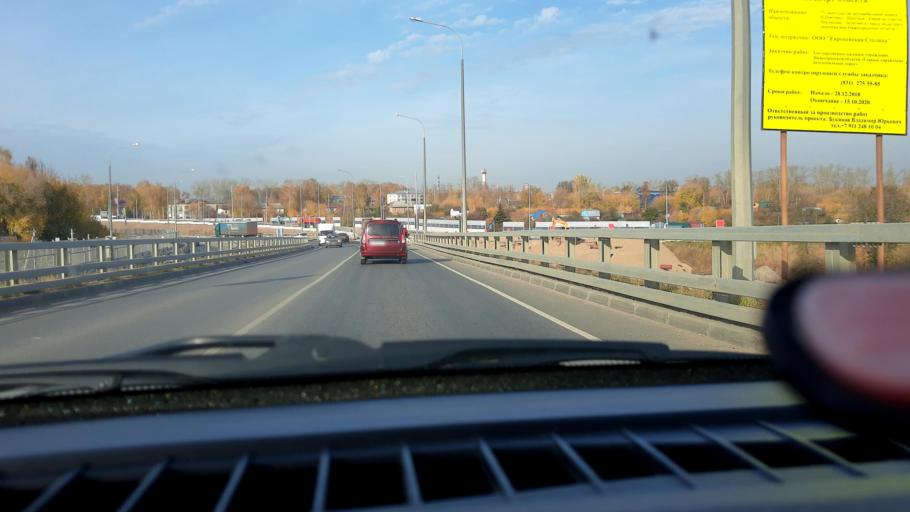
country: RU
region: Nizjnij Novgorod
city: Neklyudovo
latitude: 56.3984
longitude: 43.9906
